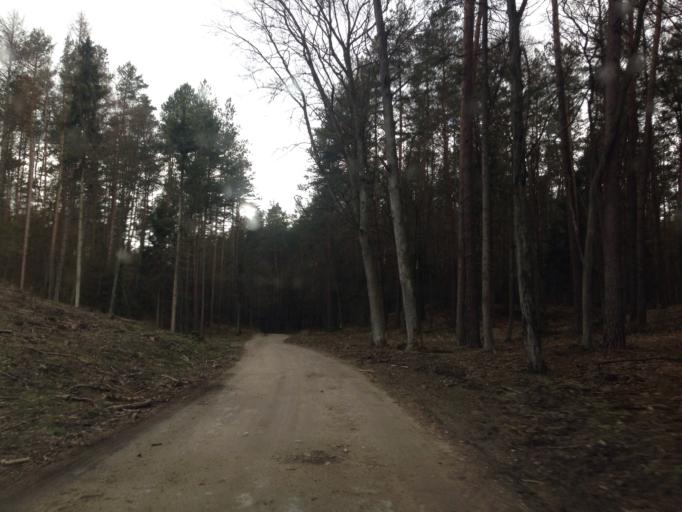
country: PL
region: Kujawsko-Pomorskie
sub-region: Powiat brodnicki
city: Gorzno
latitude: 53.1855
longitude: 19.6723
